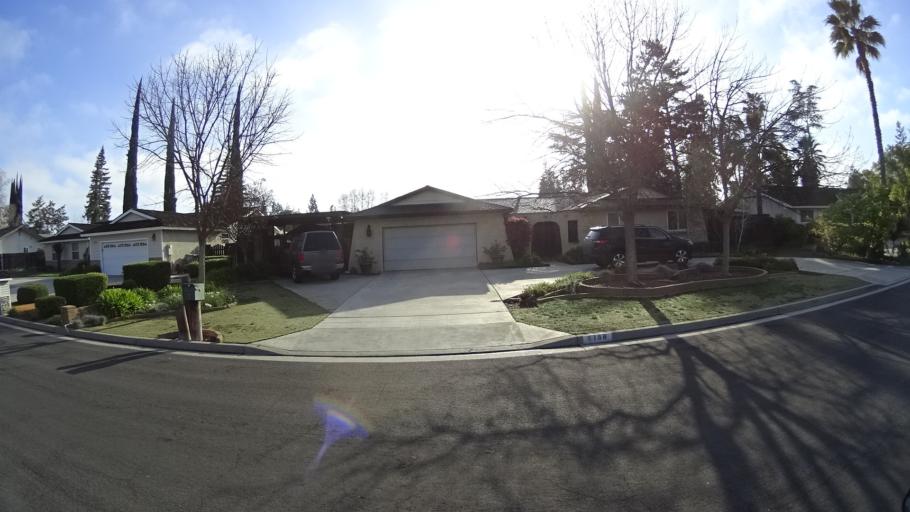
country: US
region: California
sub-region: Fresno County
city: Fresno
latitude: 36.8264
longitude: -119.8293
